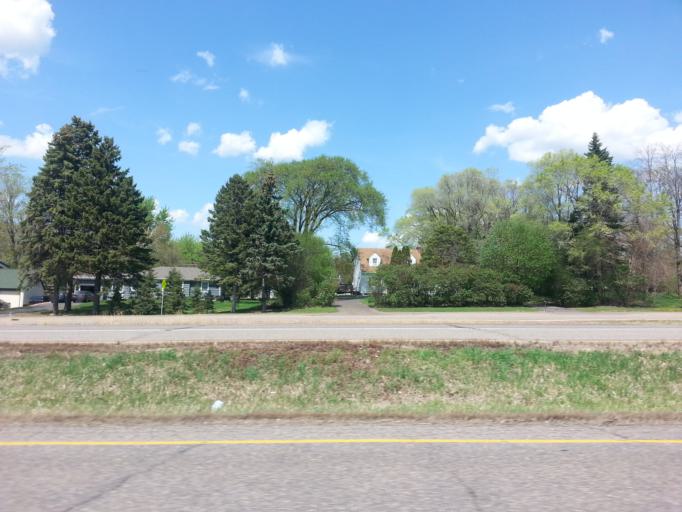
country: US
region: Minnesota
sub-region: Dakota County
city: Mendota Heights
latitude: 44.8834
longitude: -93.1167
